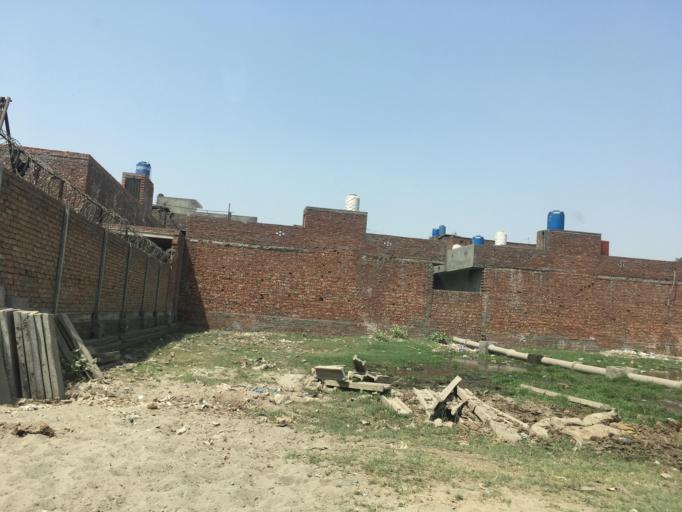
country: PK
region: Punjab
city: Lahore
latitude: 31.6113
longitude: 74.3505
